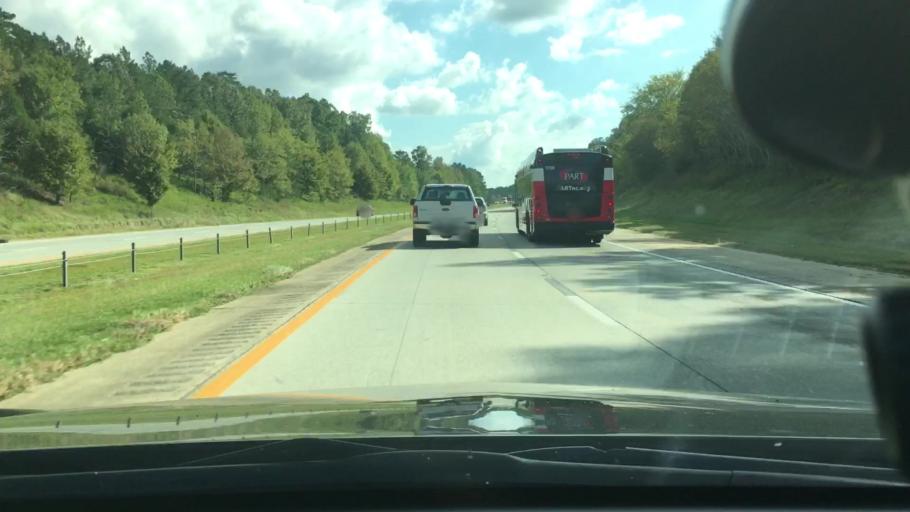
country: US
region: North Carolina
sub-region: Orange County
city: Chapel Hill
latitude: 35.9944
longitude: -79.0755
